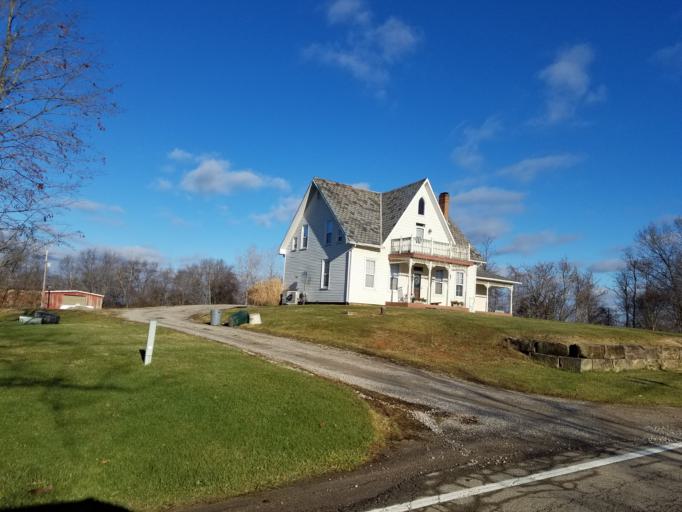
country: US
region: Ohio
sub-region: Coshocton County
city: Coshocton
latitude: 40.2516
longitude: -81.9339
